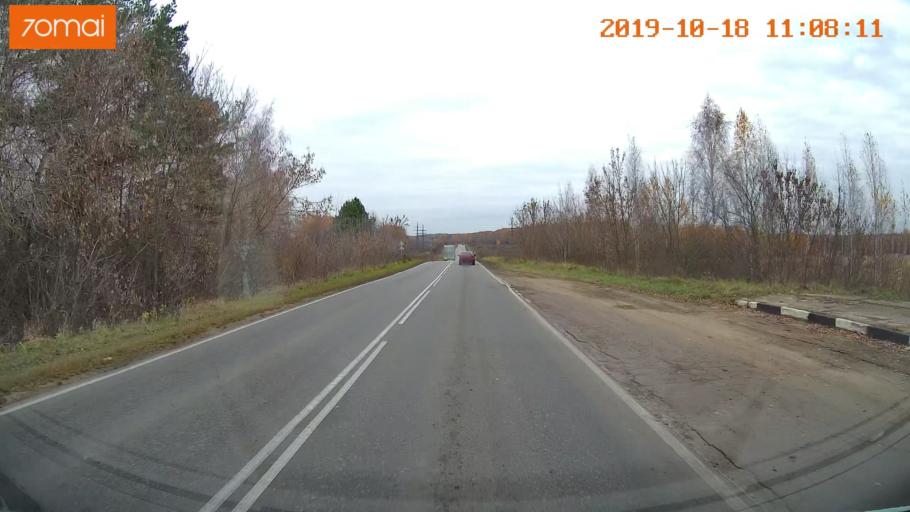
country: RU
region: Tula
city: Kimovsk
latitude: 53.9343
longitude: 38.5384
